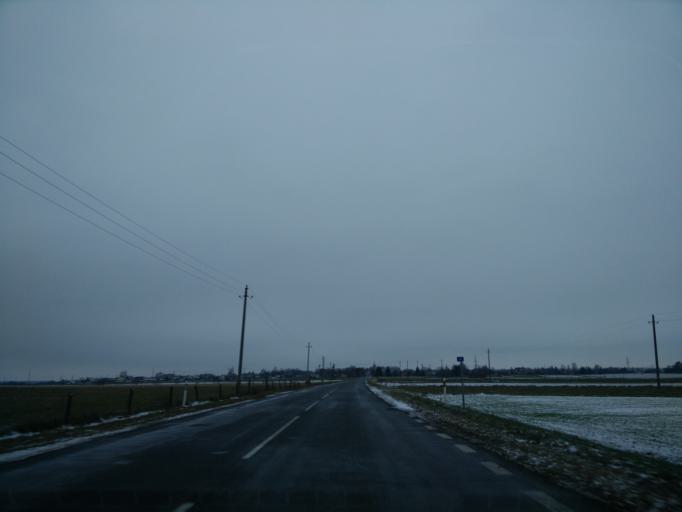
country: LT
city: Ariogala
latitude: 55.3532
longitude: 23.3804
